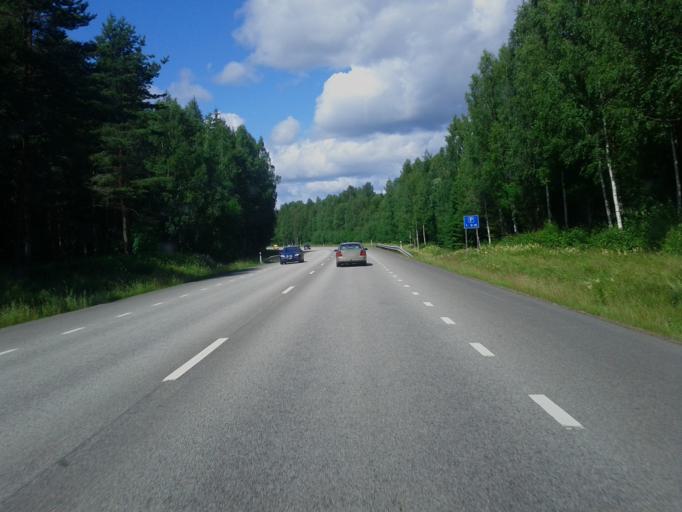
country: SE
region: Dalarna
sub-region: Rattviks Kommun
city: Raettvik
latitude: 60.9048
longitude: 15.0702
